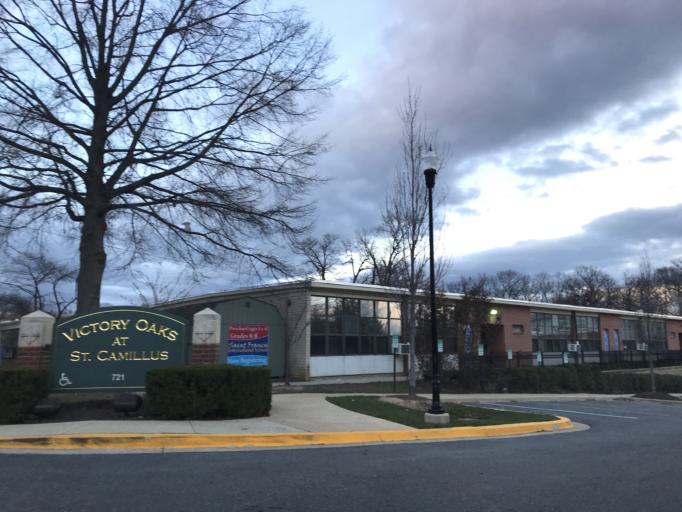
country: US
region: Maryland
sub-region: Prince George's County
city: Adelphi
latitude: 39.0095
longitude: -76.9840
